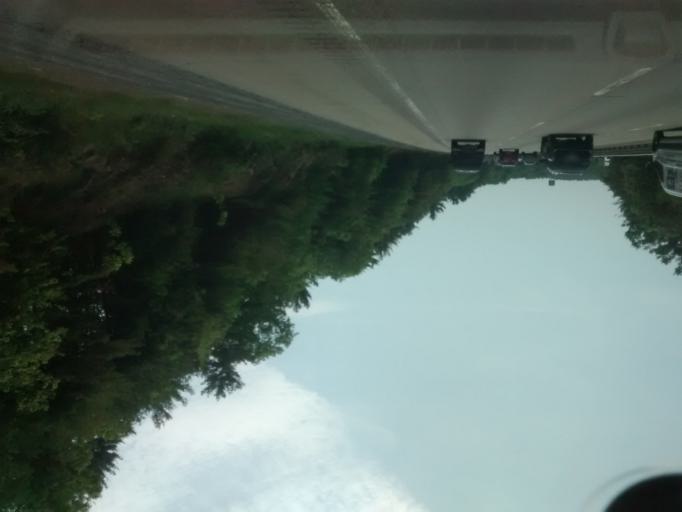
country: US
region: Massachusetts
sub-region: Norfolk County
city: Wrentham
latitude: 42.0469
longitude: -71.3622
